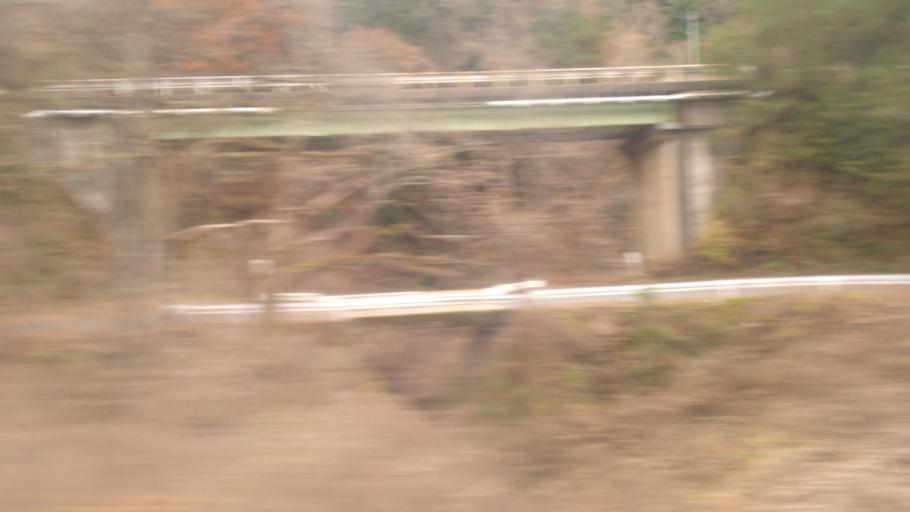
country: JP
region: Gifu
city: Nakatsugawa
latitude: 35.6640
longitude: 137.6258
